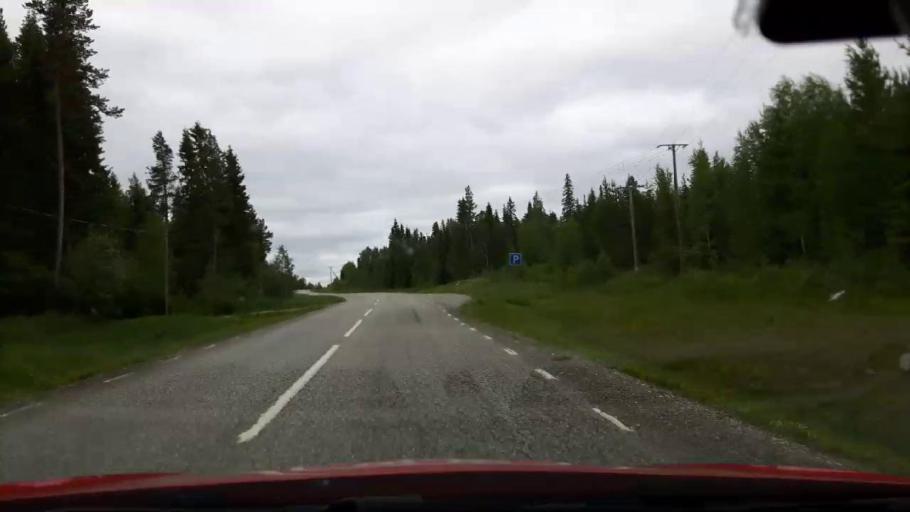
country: SE
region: Jaemtland
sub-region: Stroemsunds Kommun
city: Stroemsund
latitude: 63.3201
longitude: 15.7630
